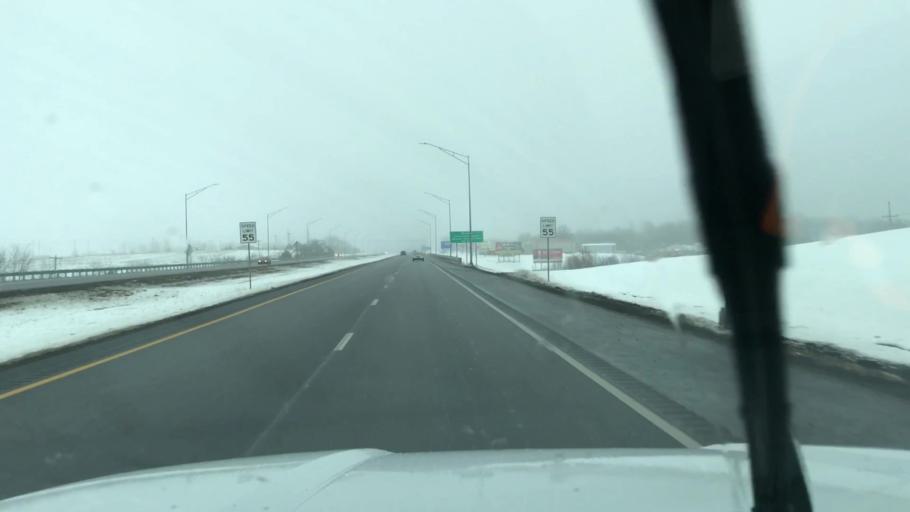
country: US
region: Missouri
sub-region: Clinton County
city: Cameron
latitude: 39.7540
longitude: -94.2494
